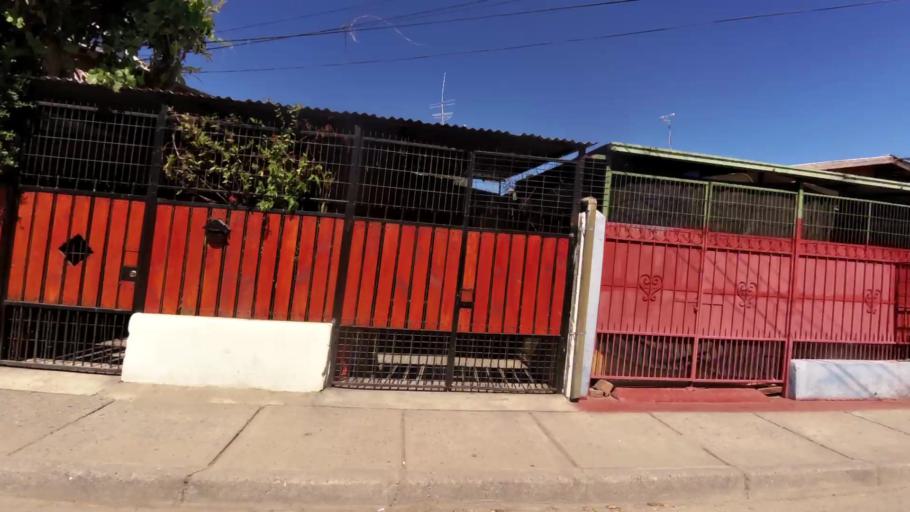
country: CL
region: O'Higgins
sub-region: Provincia de Colchagua
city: Chimbarongo
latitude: -34.5721
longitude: -70.9975
